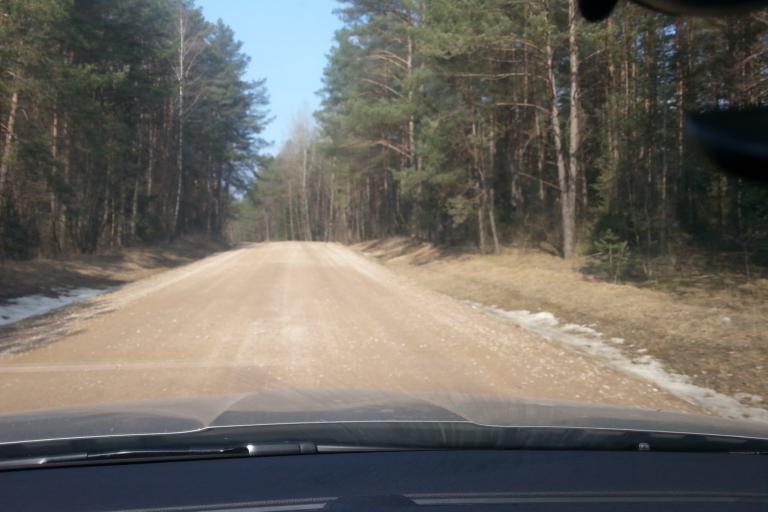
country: LT
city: Trakai
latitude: 54.5627
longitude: 24.9774
